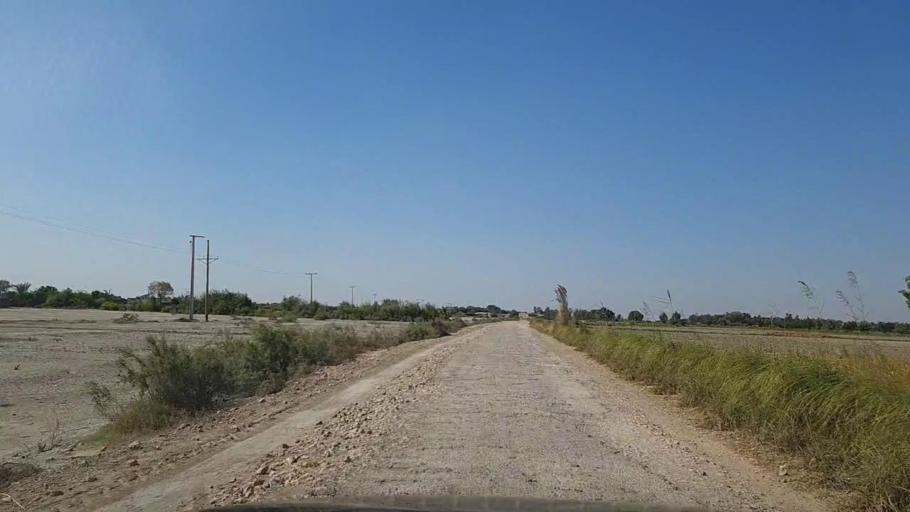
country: PK
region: Sindh
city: Mirpur Sakro
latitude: 24.6096
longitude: 67.7832
